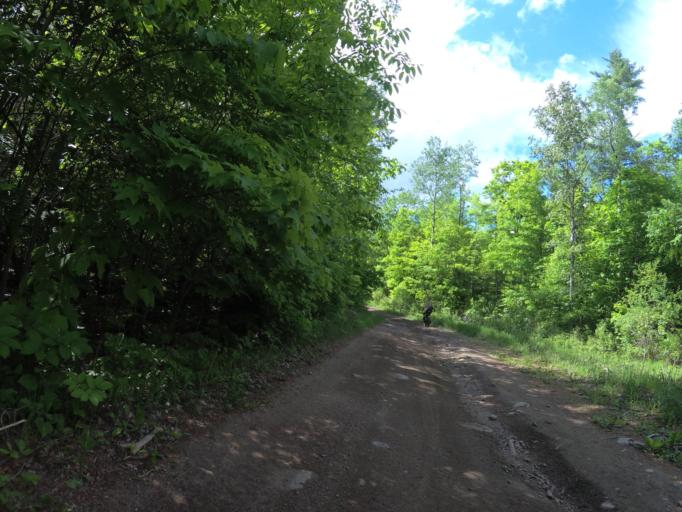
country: CA
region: Ontario
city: Renfrew
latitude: 45.1146
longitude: -76.8760
